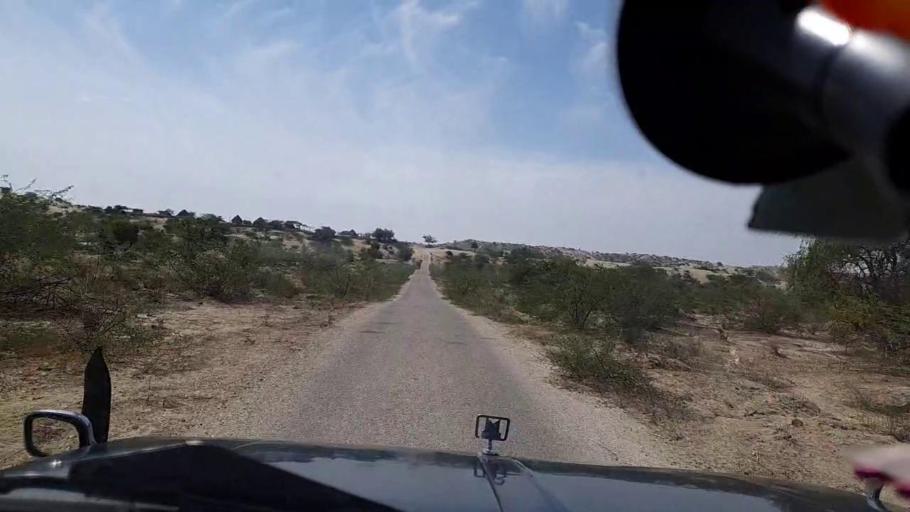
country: PK
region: Sindh
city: Diplo
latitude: 24.3736
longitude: 69.5840
